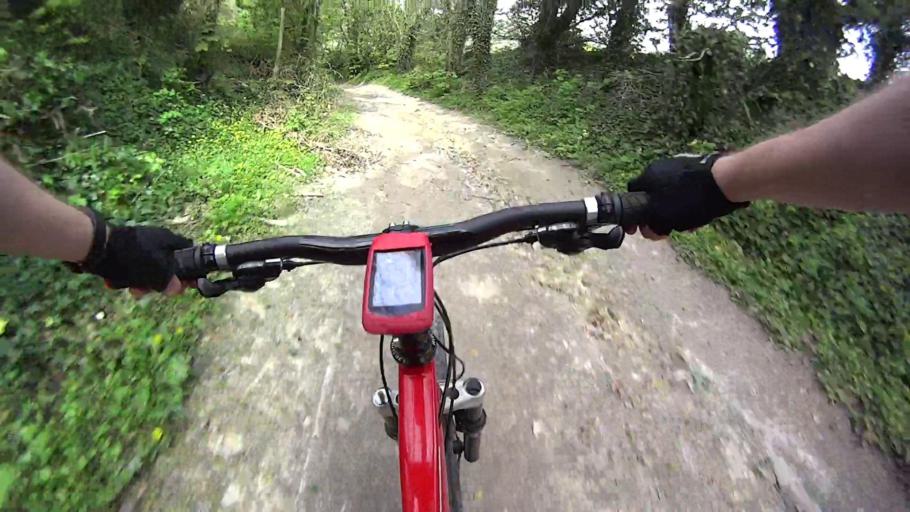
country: GB
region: England
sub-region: East Sussex
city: Seaford
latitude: 50.8093
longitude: 0.1701
